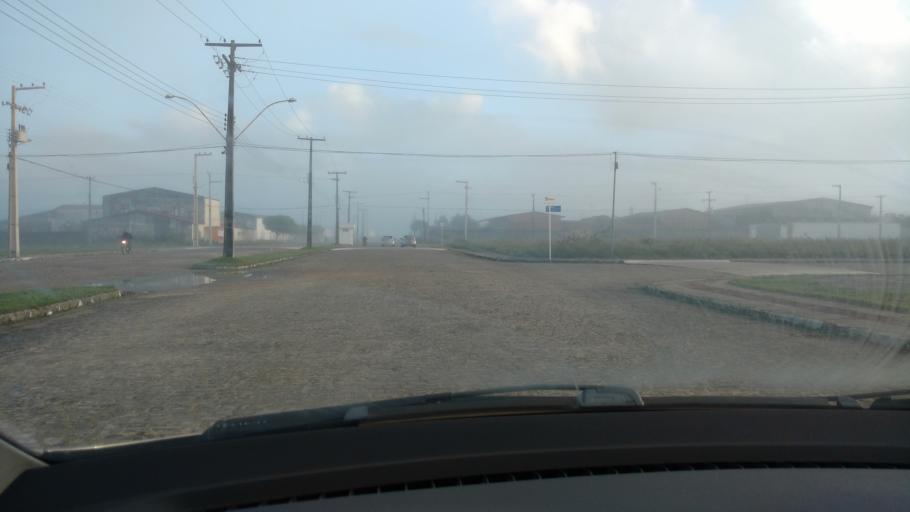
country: BR
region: Sergipe
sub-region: Tobias Barreto
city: Tobias Barreto
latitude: -11.1724
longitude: -37.9845
